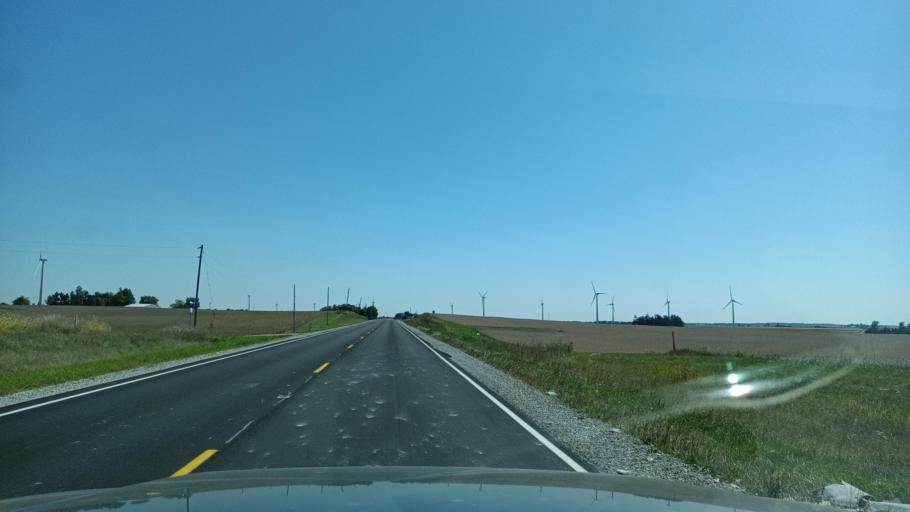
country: US
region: Illinois
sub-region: McLean County
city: Twin Grove
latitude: 40.5794
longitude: -89.0999
